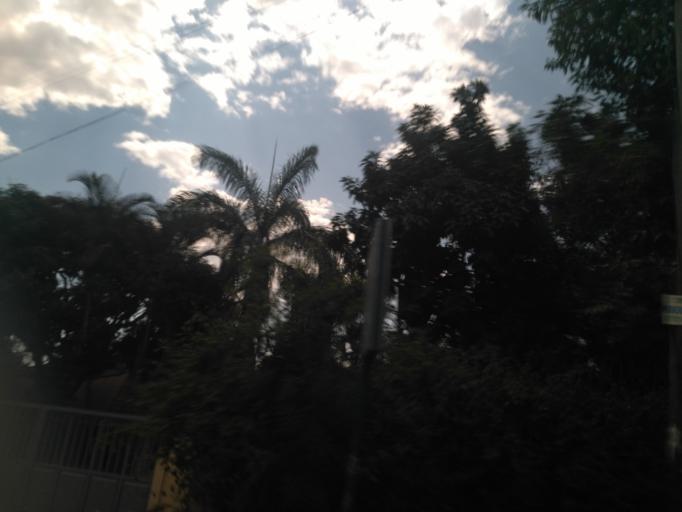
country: TZ
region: Mwanza
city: Mwanza
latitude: -2.5085
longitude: 32.9096
